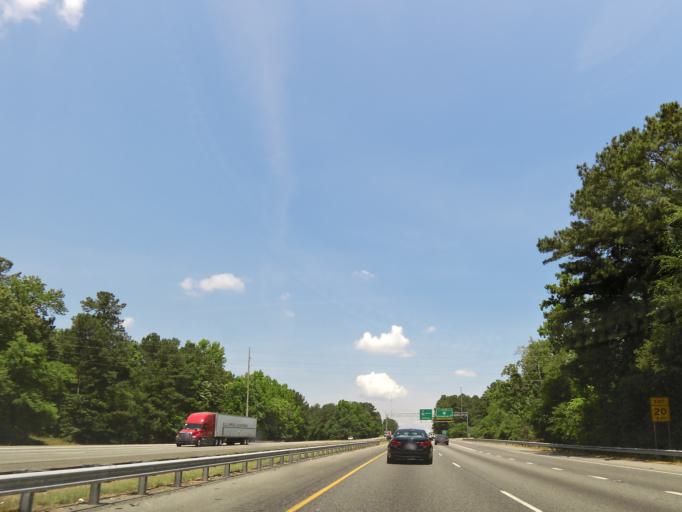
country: US
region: Georgia
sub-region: Monroe County
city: Forsyth
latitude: 32.9470
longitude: -83.8124
